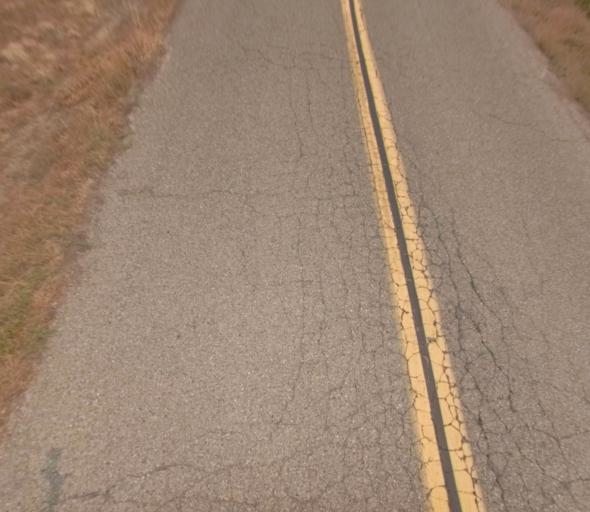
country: US
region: California
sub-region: Madera County
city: Oakhurst
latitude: 37.3460
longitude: -119.6098
